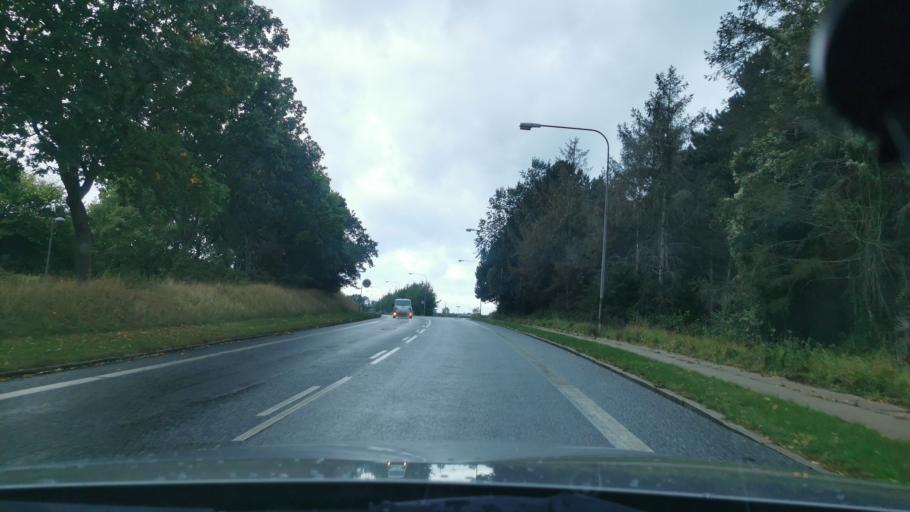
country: DK
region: Zealand
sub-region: Kalundborg Kommune
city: Kalundborg
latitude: 55.6880
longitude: 11.0672
